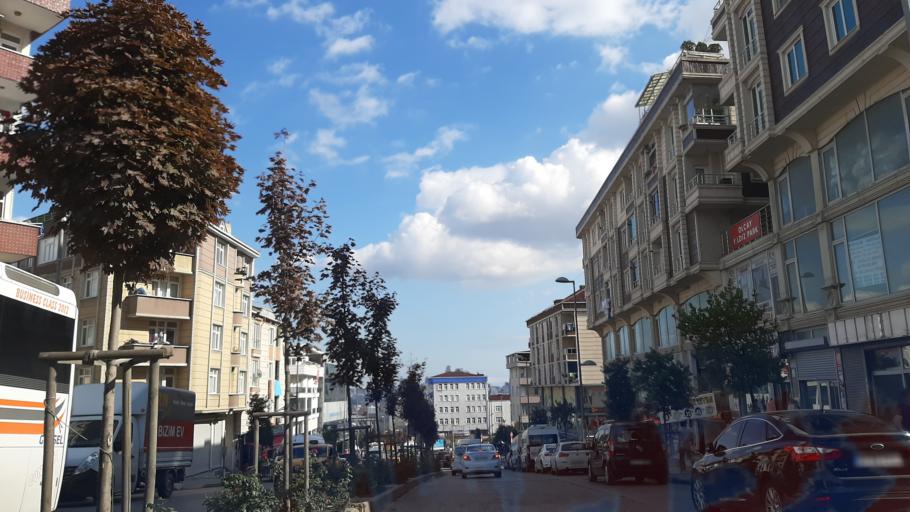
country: TR
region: Istanbul
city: Esenyurt
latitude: 41.0332
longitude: 28.6525
